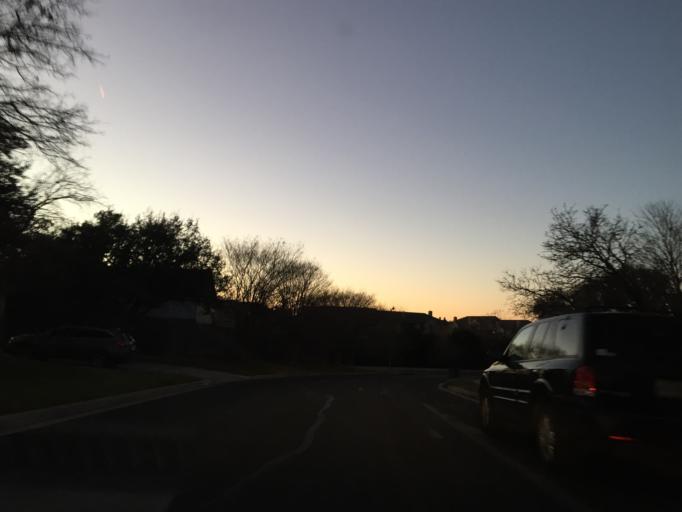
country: US
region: Texas
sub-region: Travis County
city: Wells Branch
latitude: 30.4010
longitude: -97.6950
